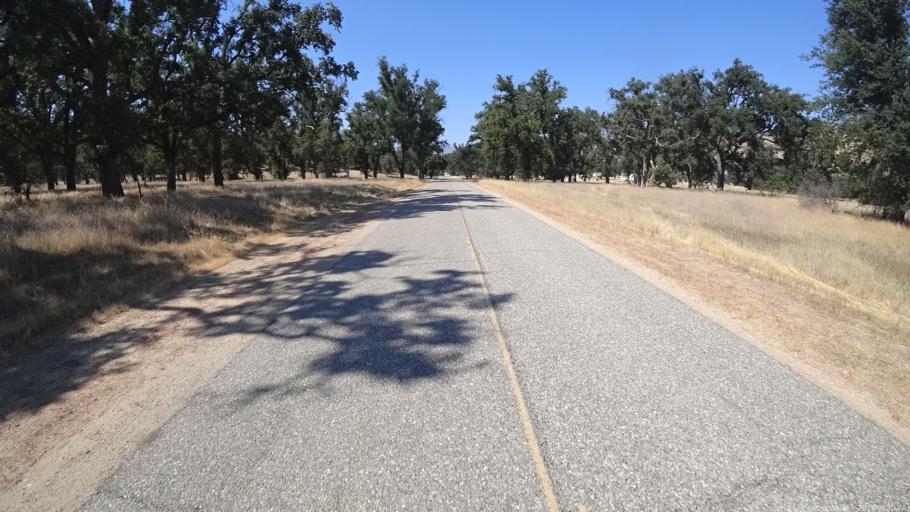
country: US
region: California
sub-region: Monterey County
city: King City
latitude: 36.0322
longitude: -121.2926
